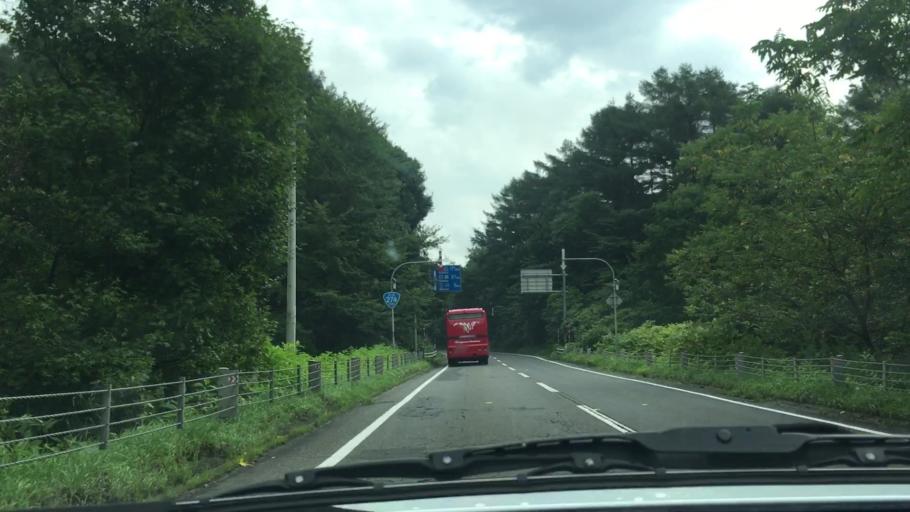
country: JP
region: Hokkaido
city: Chitose
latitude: 42.9439
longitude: 141.7456
